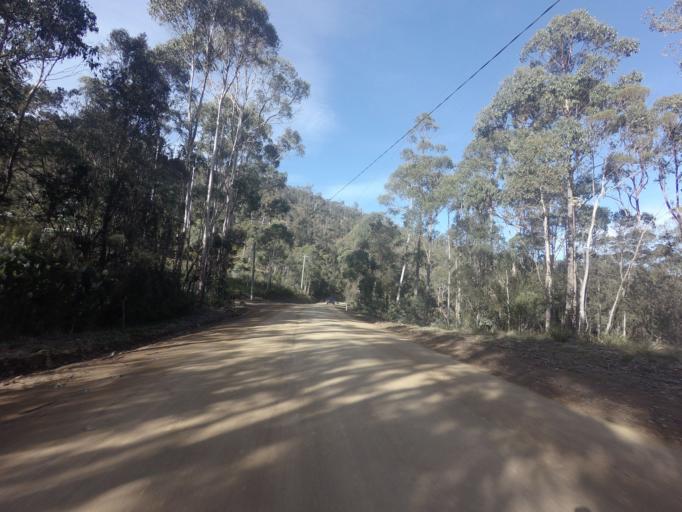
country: AU
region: Tasmania
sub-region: Huon Valley
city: Huonville
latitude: -43.0650
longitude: 147.0899
